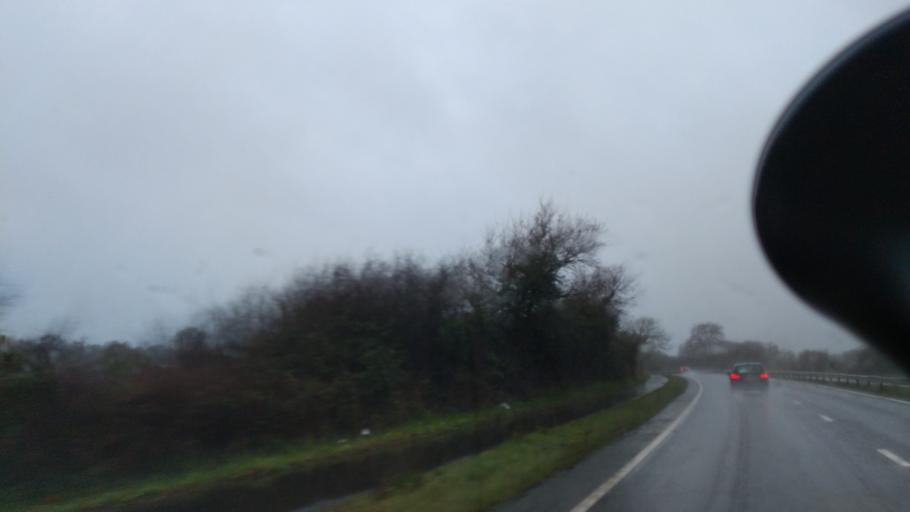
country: GB
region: England
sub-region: West Sussex
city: Rustington
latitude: 50.8413
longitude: -0.4883
